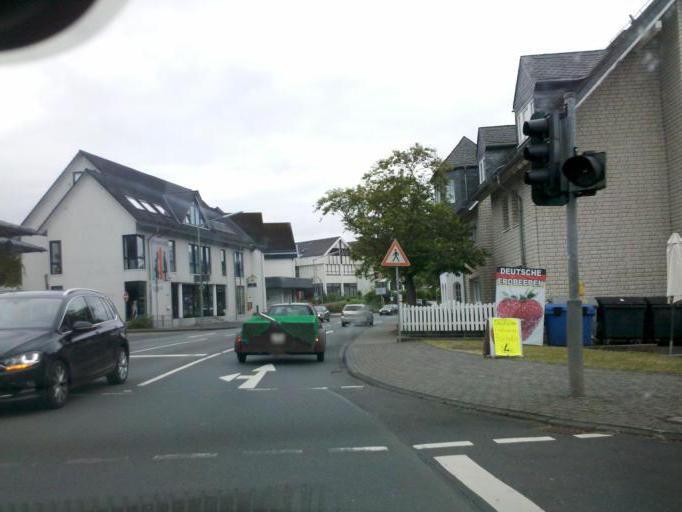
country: DE
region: North Rhine-Westphalia
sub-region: Regierungsbezirk Arnsberg
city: Wilnsdorf
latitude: 50.8193
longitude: 8.1085
